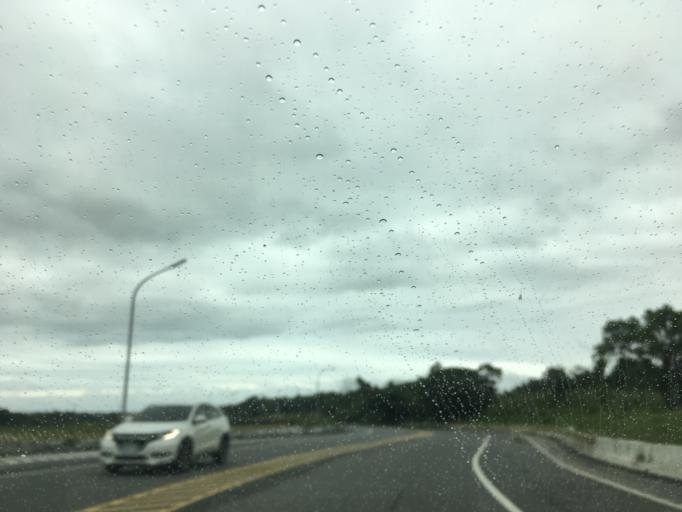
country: TW
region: Taiwan
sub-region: Hualien
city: Hualian
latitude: 24.0032
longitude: 121.5765
